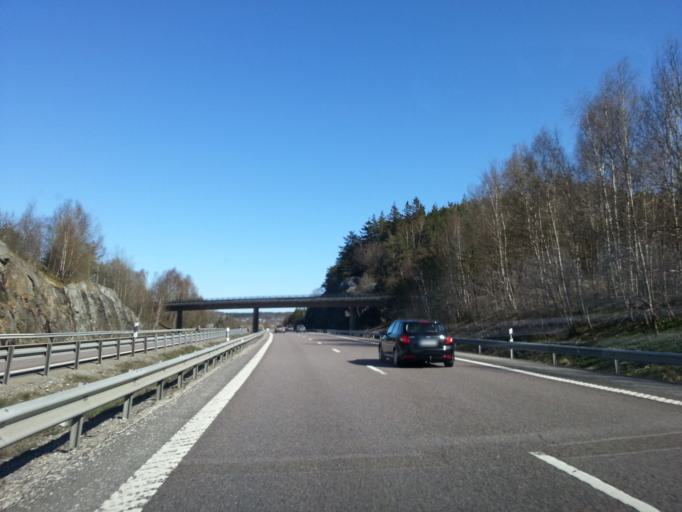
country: SE
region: Vaestra Goetaland
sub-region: Stenungsunds Kommun
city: Stora Hoga
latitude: 58.0041
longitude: 11.8447
